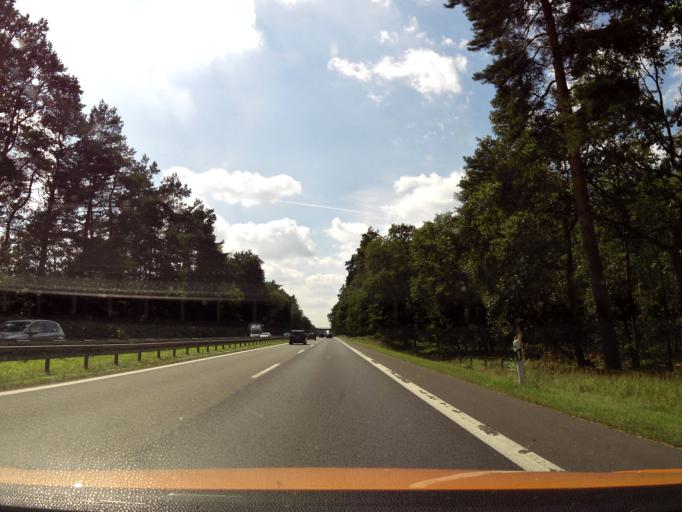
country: DE
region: Brandenburg
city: Althuttendorf
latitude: 52.9244
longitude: 13.7753
